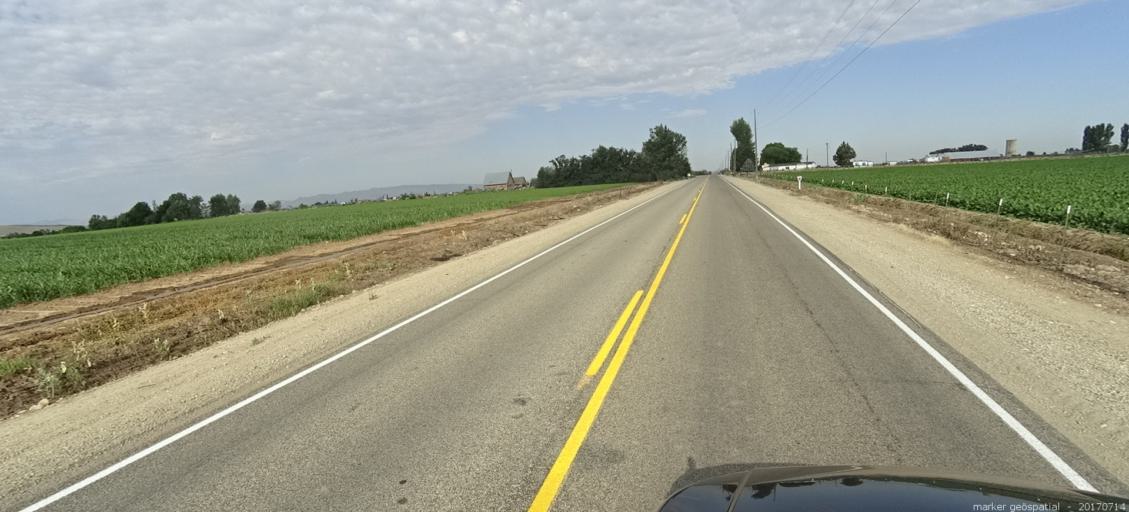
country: US
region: Idaho
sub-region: Ada County
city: Kuna
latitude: 43.4884
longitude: -116.4413
